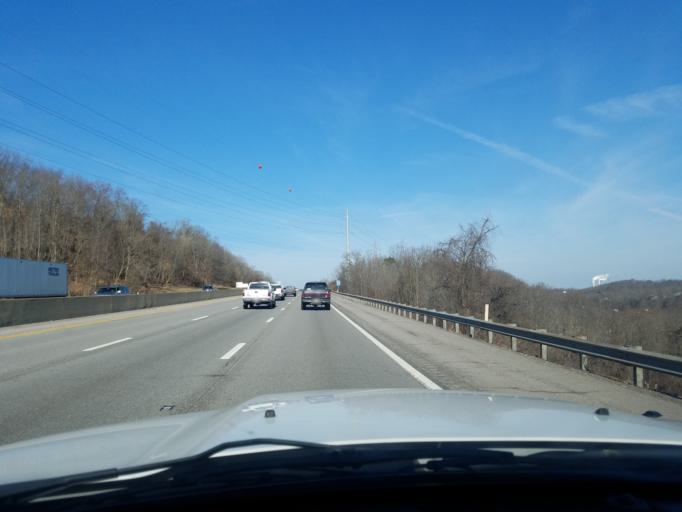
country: US
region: West Virginia
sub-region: Kanawha County
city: Cross Lanes
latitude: 38.4182
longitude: -81.8013
